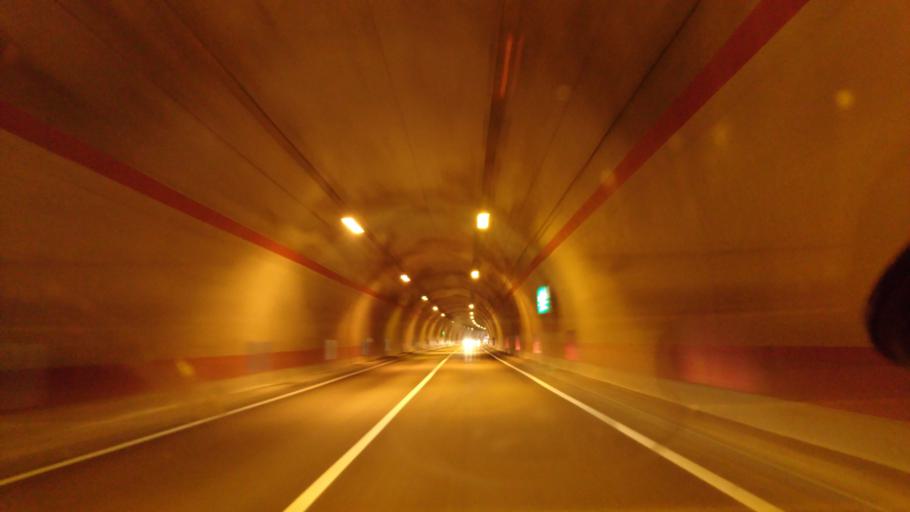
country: IT
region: Liguria
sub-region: Provincia di Savona
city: Carcare
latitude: 44.3479
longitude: 8.3126
